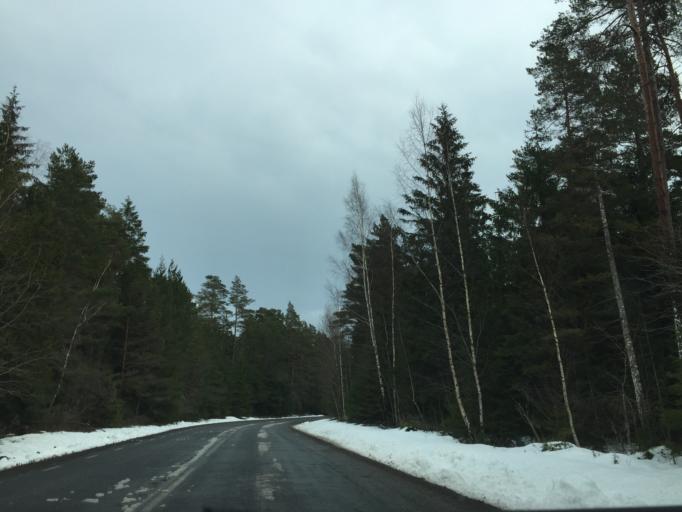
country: EE
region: Saare
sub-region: Kuressaare linn
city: Kuressaare
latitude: 58.5958
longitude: 22.5956
